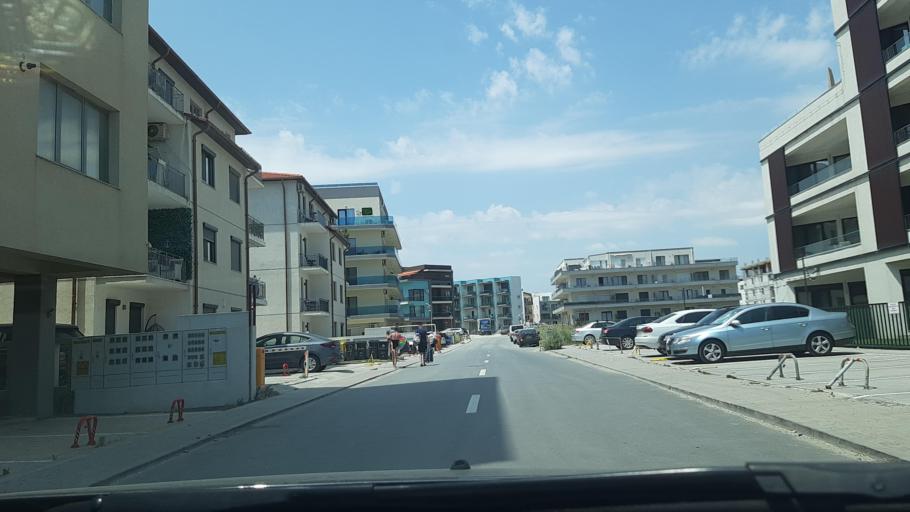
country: RO
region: Constanta
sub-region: Comuna Navodari
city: Navodari
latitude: 44.2922
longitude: 28.6236
